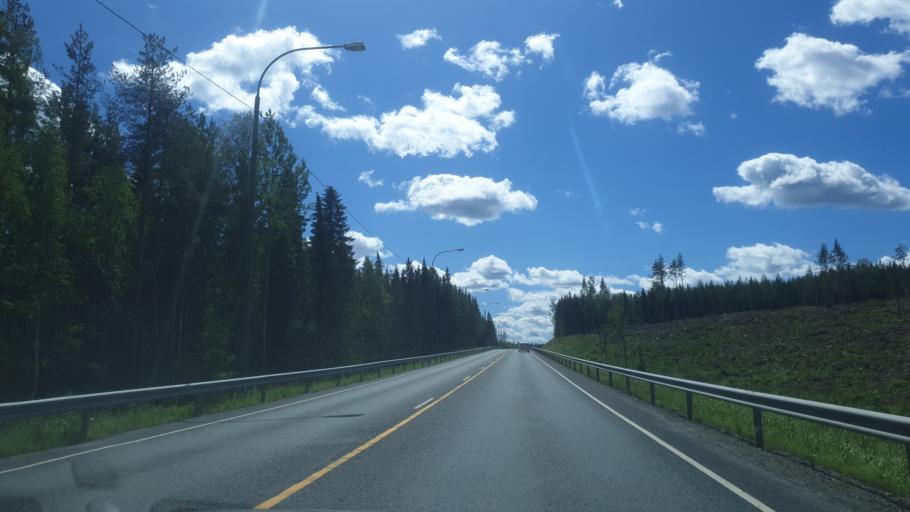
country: FI
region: Northern Savo
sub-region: Varkaus
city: Leppaevirta
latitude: 62.6147
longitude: 27.6229
